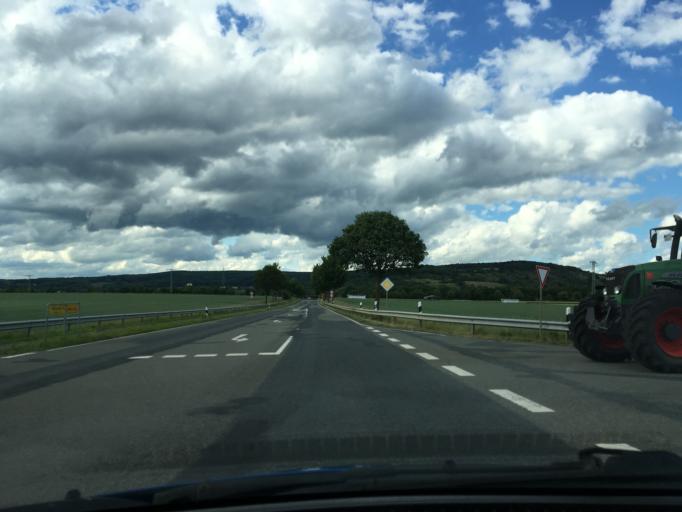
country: DE
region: Lower Saxony
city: Einbeck
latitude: 51.7990
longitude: 9.8982
